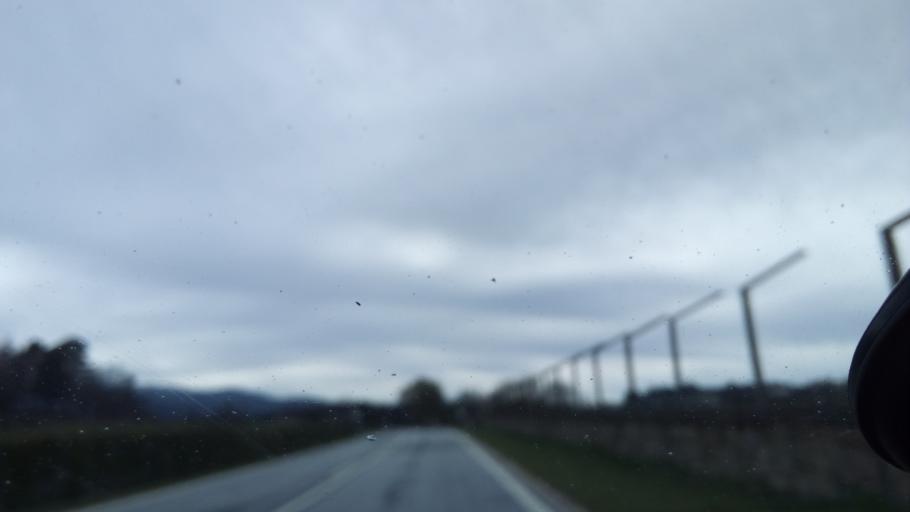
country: PT
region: Guarda
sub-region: Seia
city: Seia
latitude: 40.4940
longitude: -7.6570
